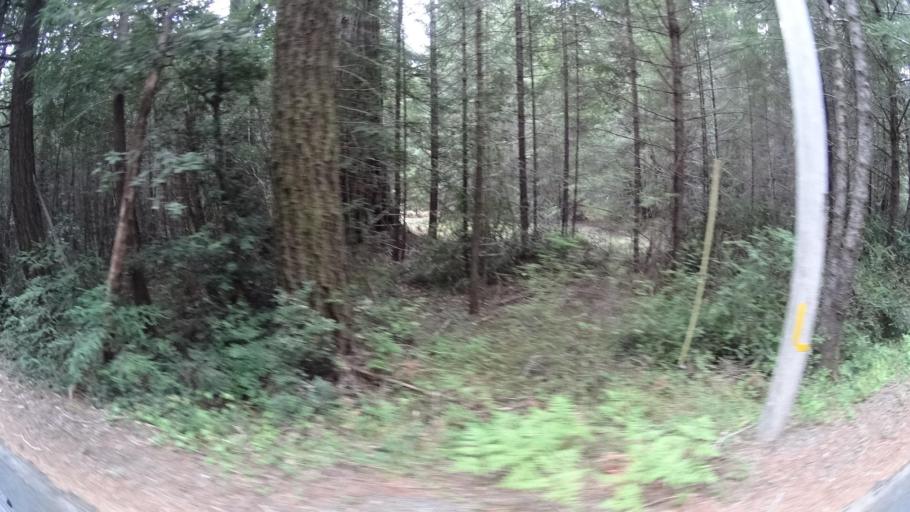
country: US
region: California
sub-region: Humboldt County
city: Redway
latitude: 39.9978
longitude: -123.9278
